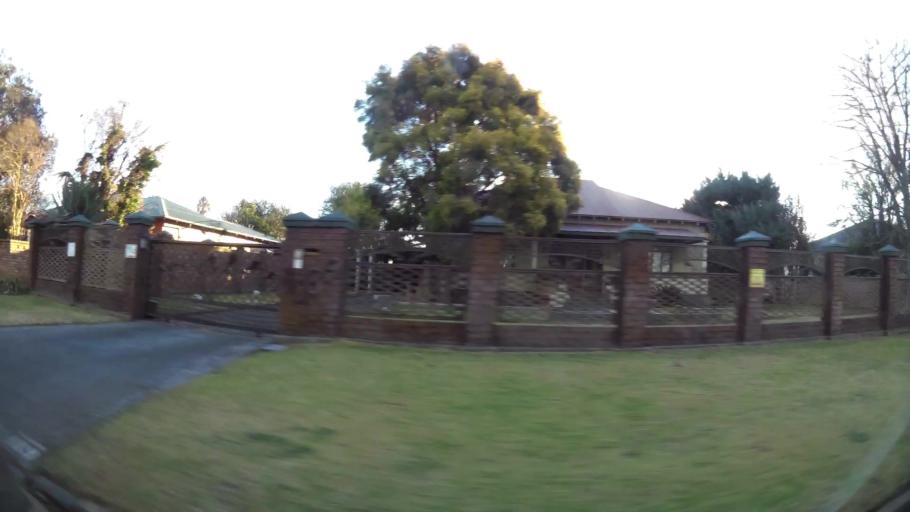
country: ZA
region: North-West
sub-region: Dr Kenneth Kaunda District Municipality
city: Potchefstroom
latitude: -26.7234
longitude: 27.0922
